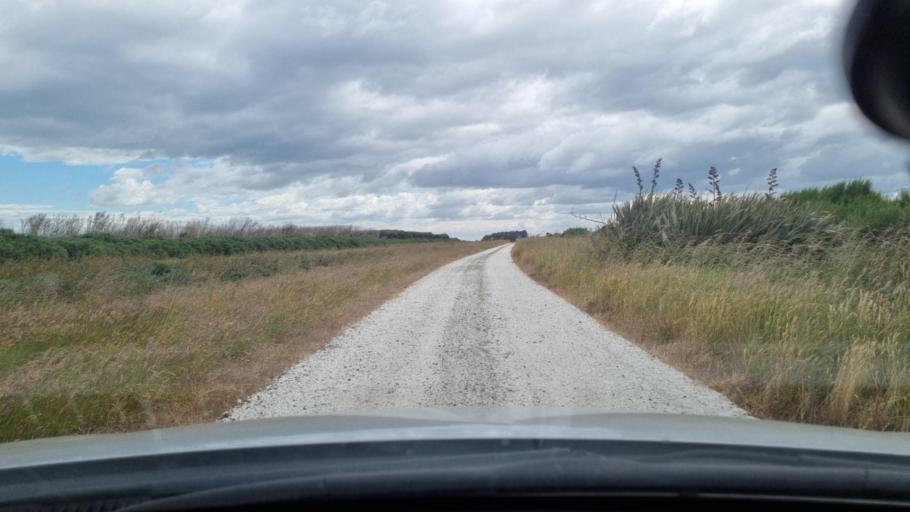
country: NZ
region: Southland
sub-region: Invercargill City
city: Bluff
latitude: -46.5299
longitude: 168.3058
